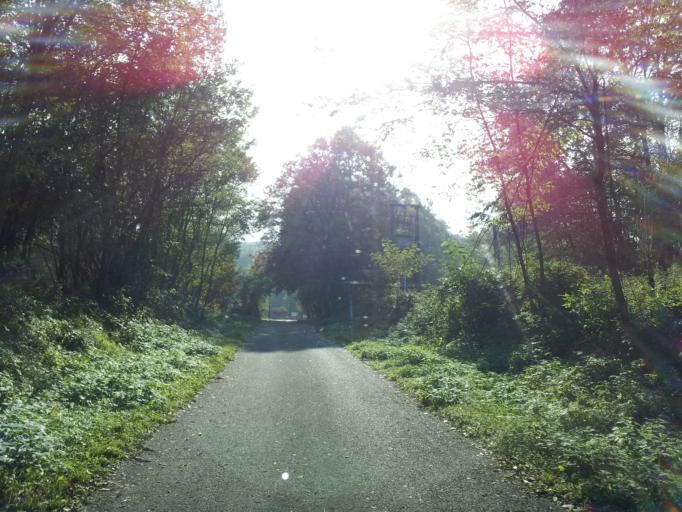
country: HU
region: Gyor-Moson-Sopron
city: Bakonyszentlaszlo
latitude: 47.3610
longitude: 17.8189
